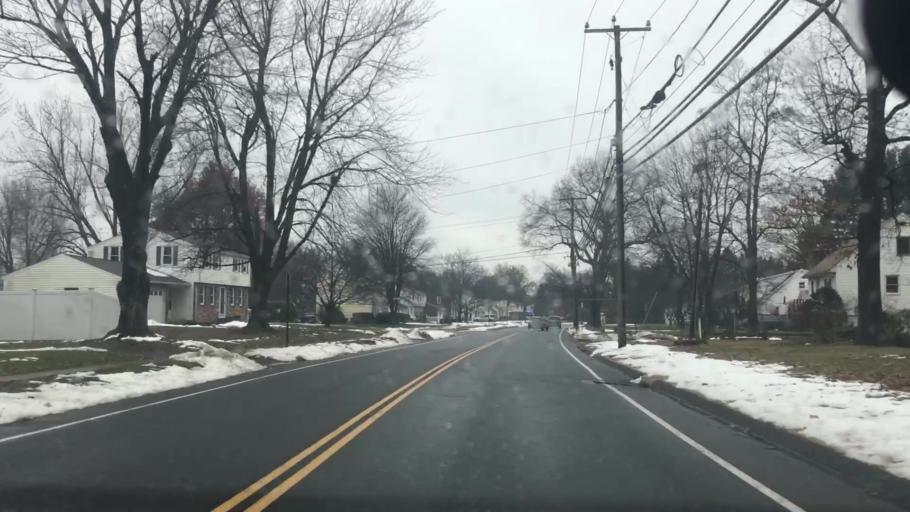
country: US
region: Connecticut
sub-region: Hartford County
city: Sherwood Manor
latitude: 42.0146
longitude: -72.5786
